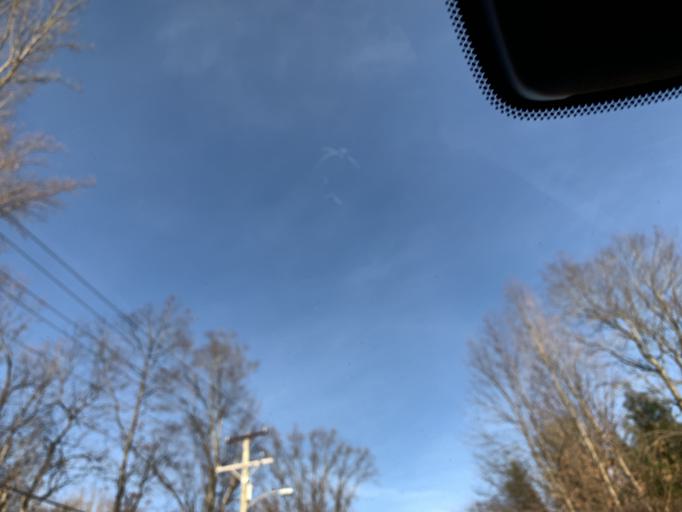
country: US
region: Virginia
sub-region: Fairfax County
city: Lake Barcroft
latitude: 38.8491
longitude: -77.1740
